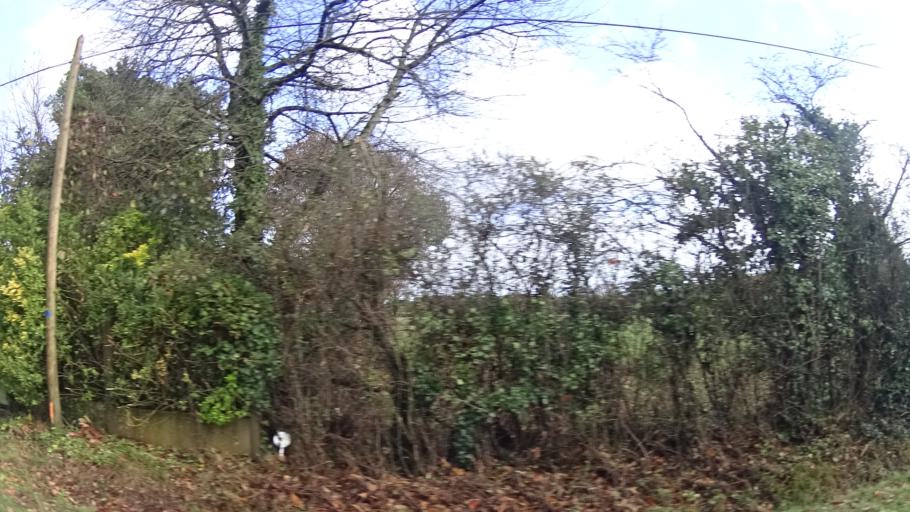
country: FR
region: Pays de la Loire
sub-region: Departement de la Loire-Atlantique
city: Saint-Nicolas-de-Redon
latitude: 47.6124
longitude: -2.0671
